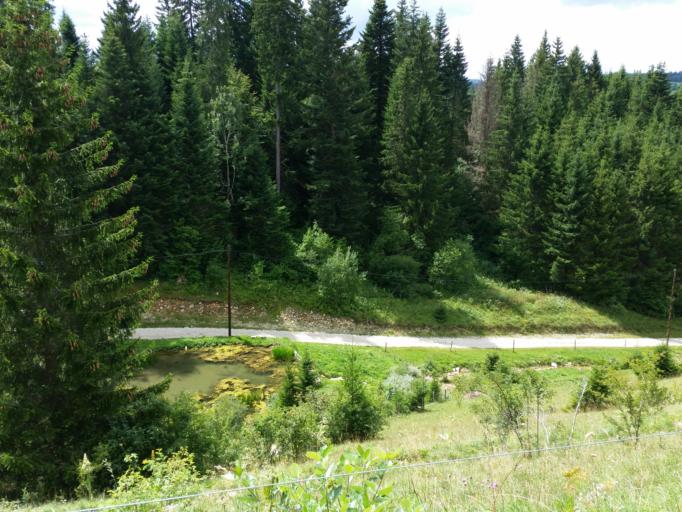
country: FR
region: Franche-Comte
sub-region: Departement du Doubs
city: Jougne
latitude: 46.7507
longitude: 6.3206
